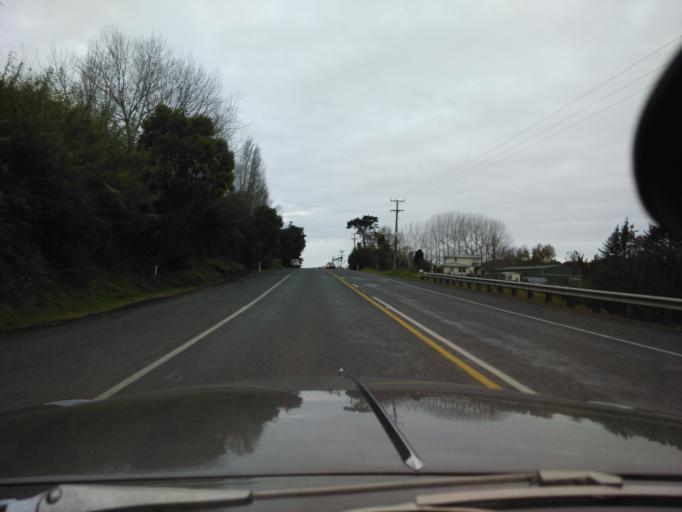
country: NZ
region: Auckland
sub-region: Auckland
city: Rothesay Bay
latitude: -36.6823
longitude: 174.6535
